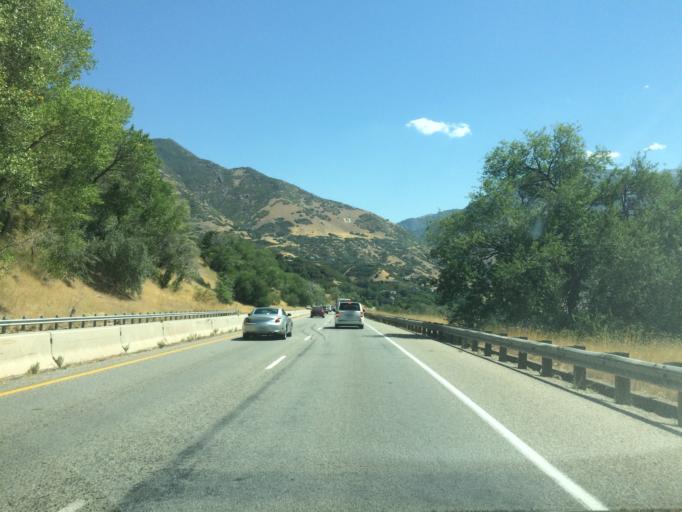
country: US
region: Utah
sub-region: Weber County
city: Uintah
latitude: 41.1480
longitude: -111.9291
